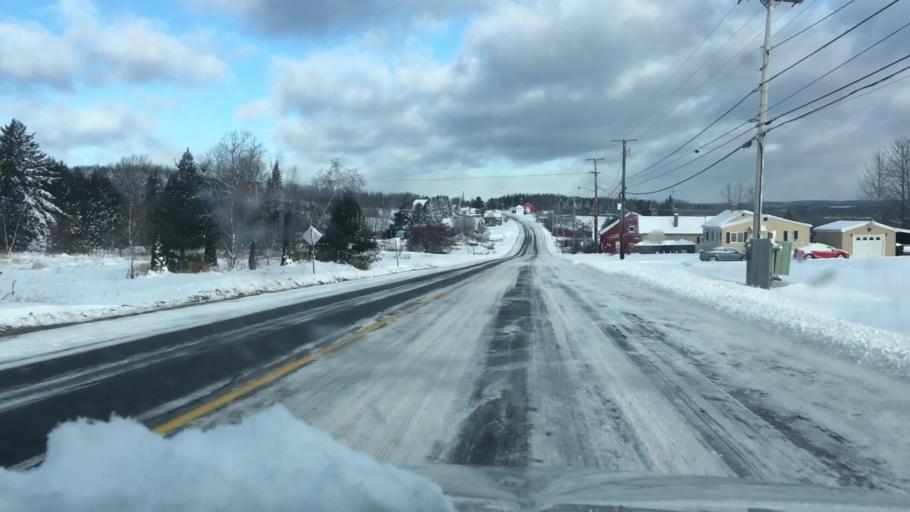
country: US
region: Maine
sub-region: Aroostook County
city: Caribou
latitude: 46.9552
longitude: -68.0276
